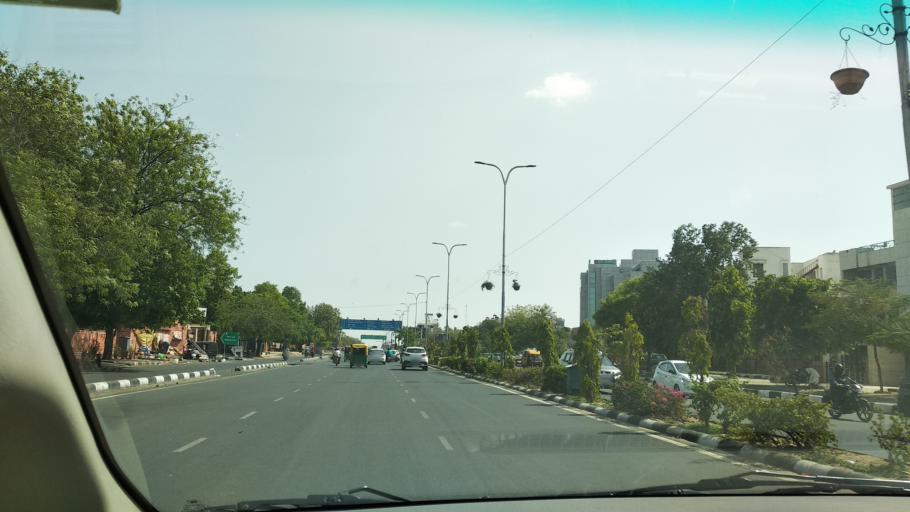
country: IN
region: Rajasthan
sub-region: Jaipur
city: Jaipur
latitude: 26.8969
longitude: 75.8157
